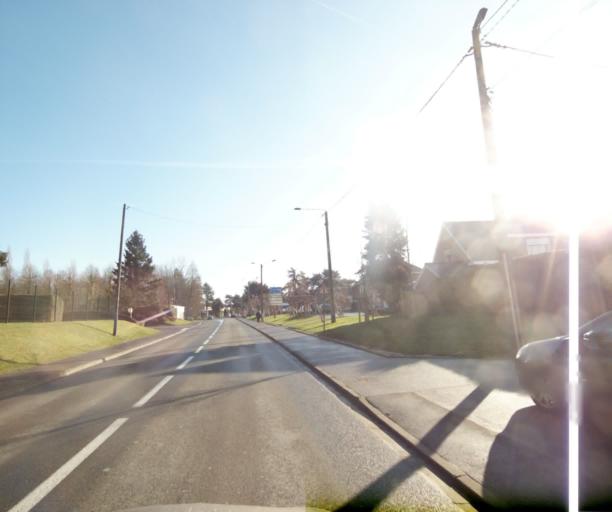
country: FR
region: Nord-Pas-de-Calais
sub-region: Departement du Nord
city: Marly
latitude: 50.3427
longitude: 3.5476
